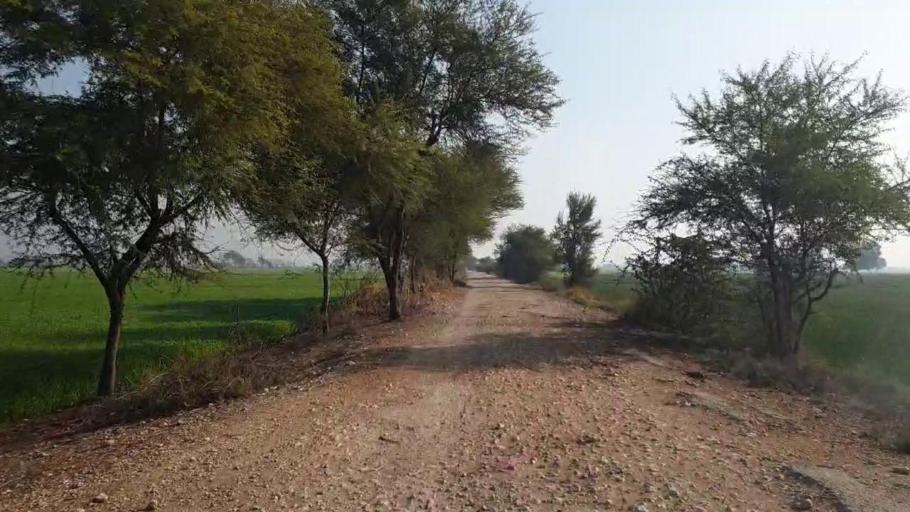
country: PK
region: Sindh
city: Shahdadpur
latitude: 26.0009
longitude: 68.6236
